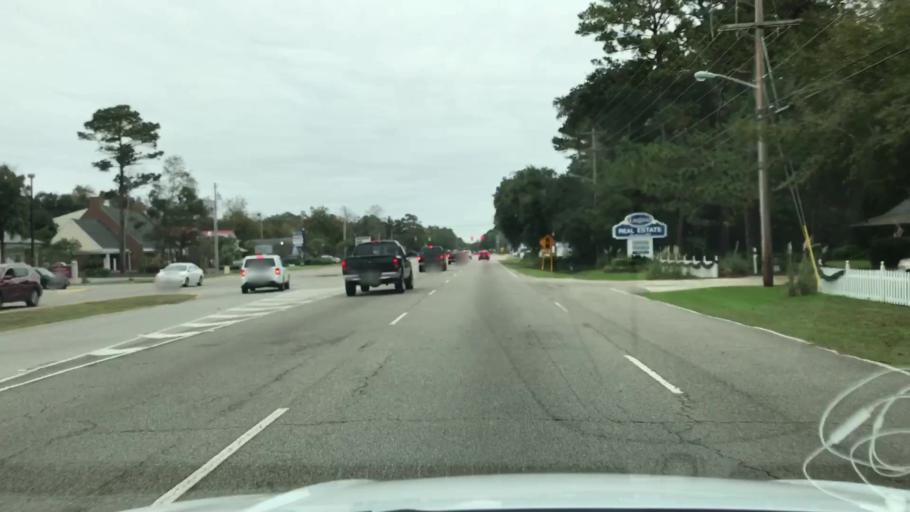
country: US
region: South Carolina
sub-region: Georgetown County
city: Murrells Inlet
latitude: 33.4695
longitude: -79.1062
